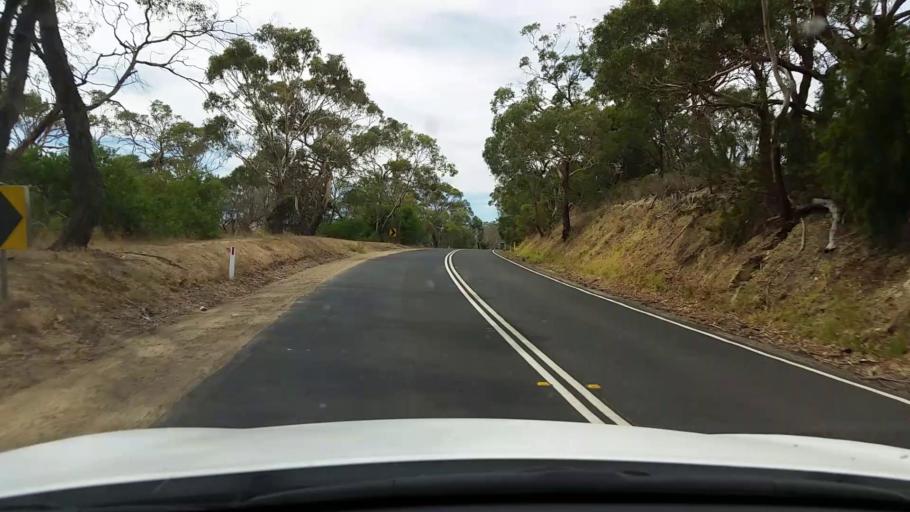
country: AU
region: Victoria
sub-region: Mornington Peninsula
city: Mount Martha
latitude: -38.2961
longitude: 145.0460
